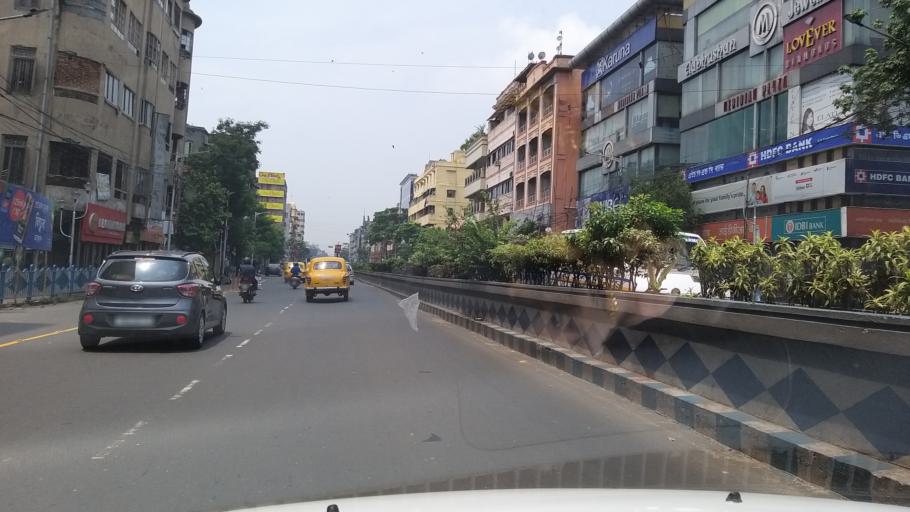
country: IN
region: West Bengal
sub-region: Kolkata
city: Bara Bazar
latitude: 22.5857
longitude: 88.3626
